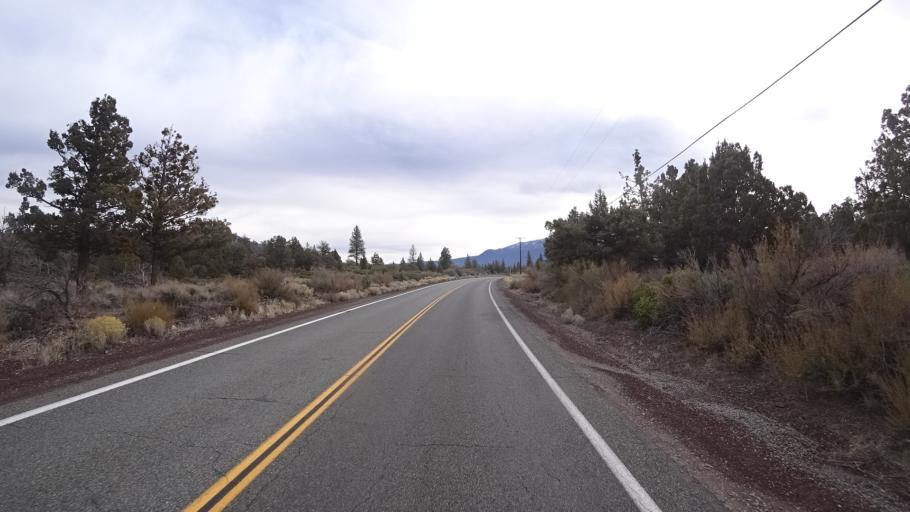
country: US
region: California
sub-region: Siskiyou County
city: Weed
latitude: 41.5514
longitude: -122.2499
